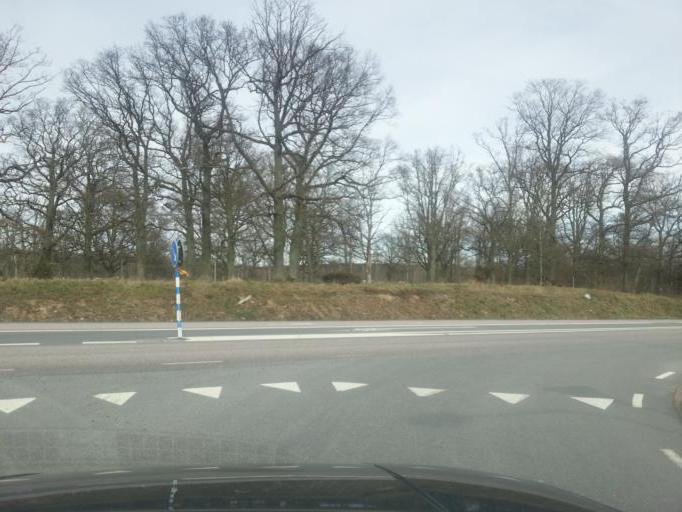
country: SE
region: Joenkoeping
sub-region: Habo Kommun
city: Habo
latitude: 57.8995
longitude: 14.0860
